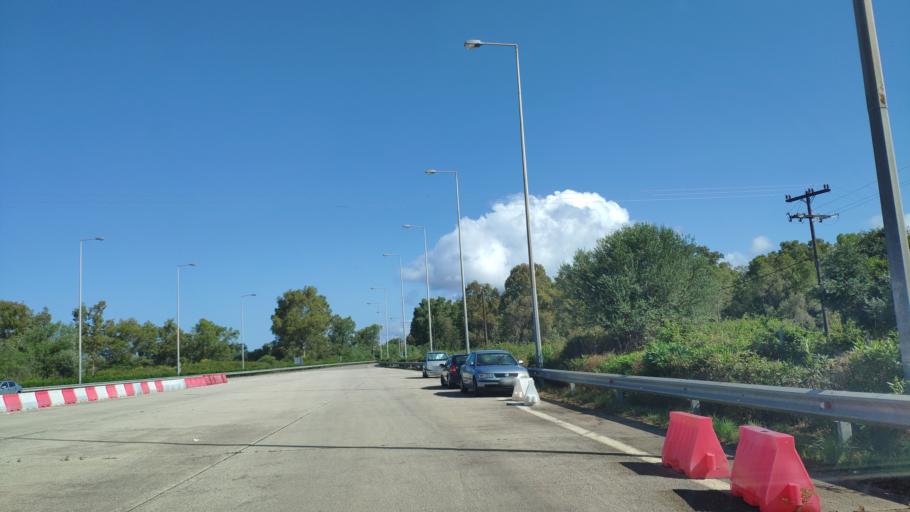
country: GR
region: Epirus
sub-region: Nomos Prevezis
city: Preveza
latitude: 38.9403
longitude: 20.7662
